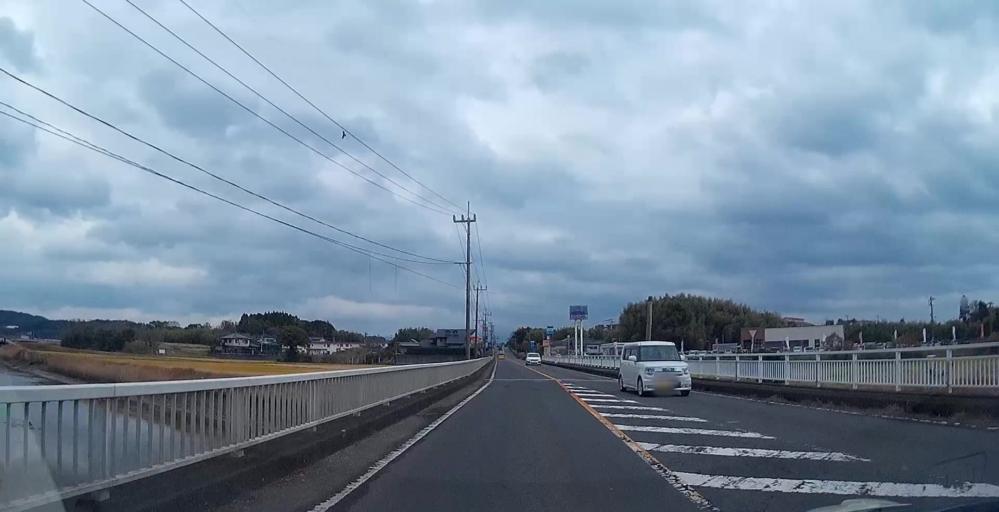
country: JP
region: Kagoshima
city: Akune
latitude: 32.0834
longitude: 130.1990
